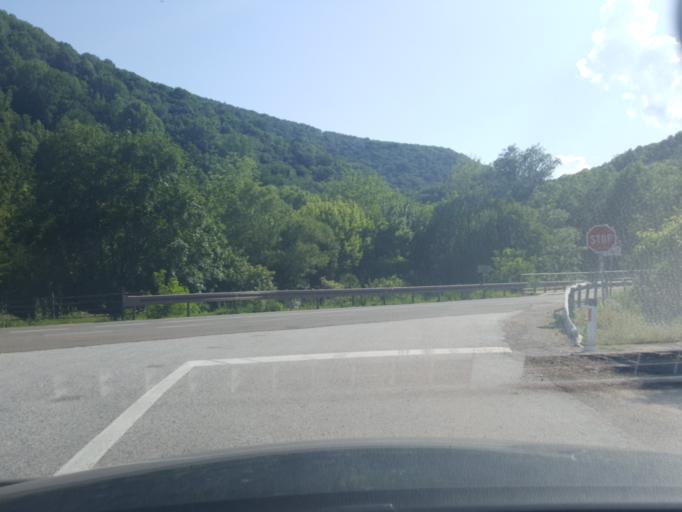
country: RS
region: Central Serbia
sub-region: Nisavski Okrug
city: Razanj
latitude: 43.8598
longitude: 21.6244
